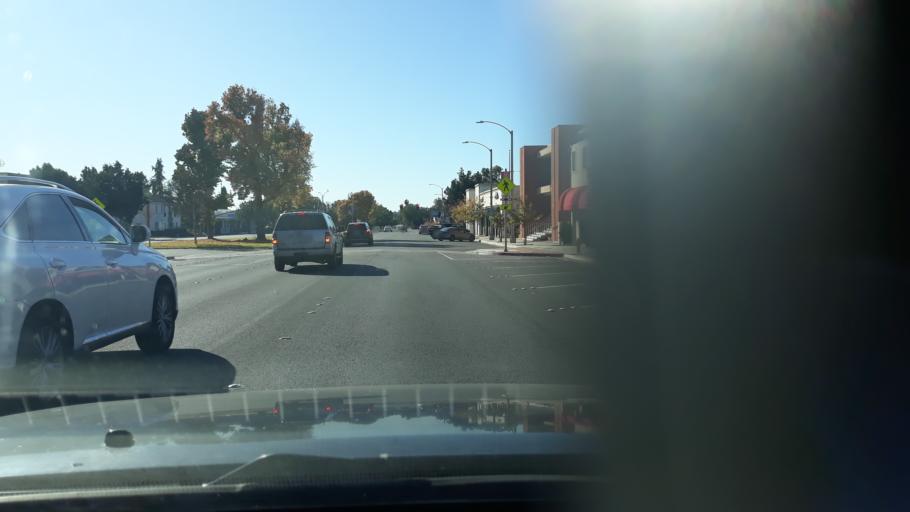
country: US
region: California
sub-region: Los Angeles County
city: San Marino
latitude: 34.1227
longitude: -118.1045
